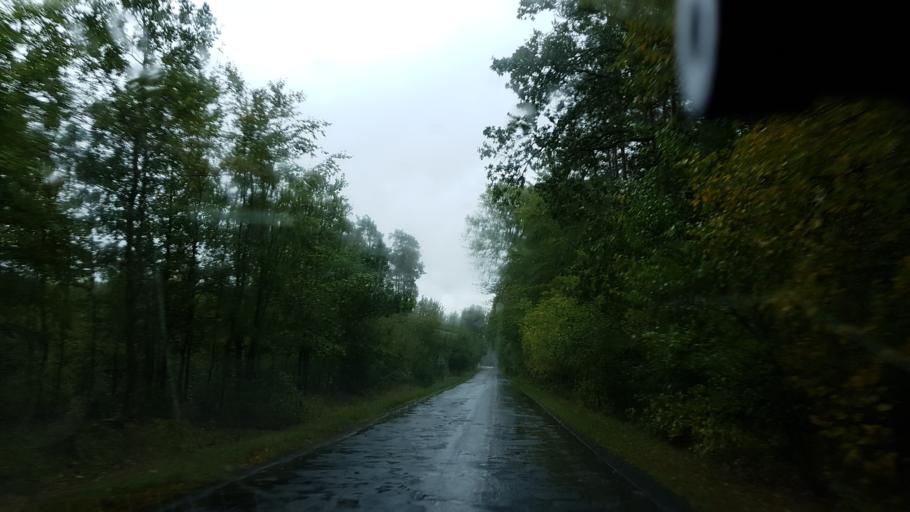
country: PL
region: West Pomeranian Voivodeship
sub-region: Powiat goleniowski
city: Przybiernow
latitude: 53.6711
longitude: 14.7351
